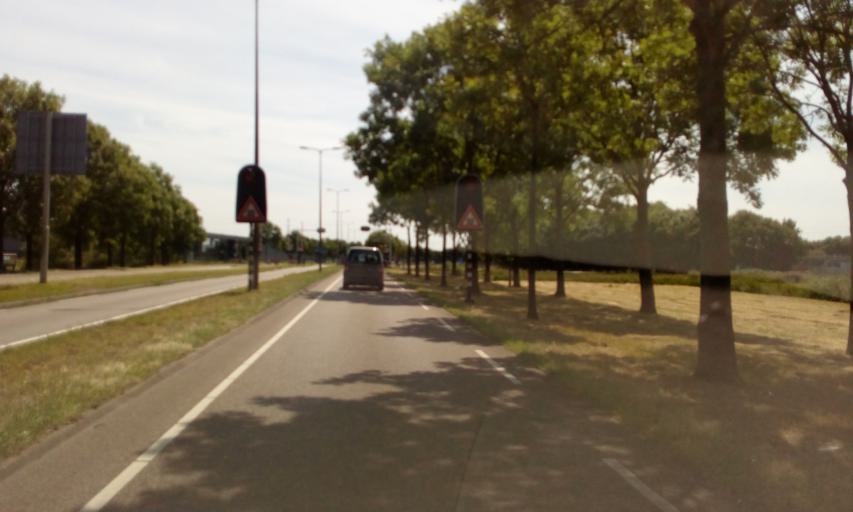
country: NL
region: South Holland
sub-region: Gemeente Alphen aan den Rijn
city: Alphen aan den Rijn
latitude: 52.1299
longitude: 4.6279
